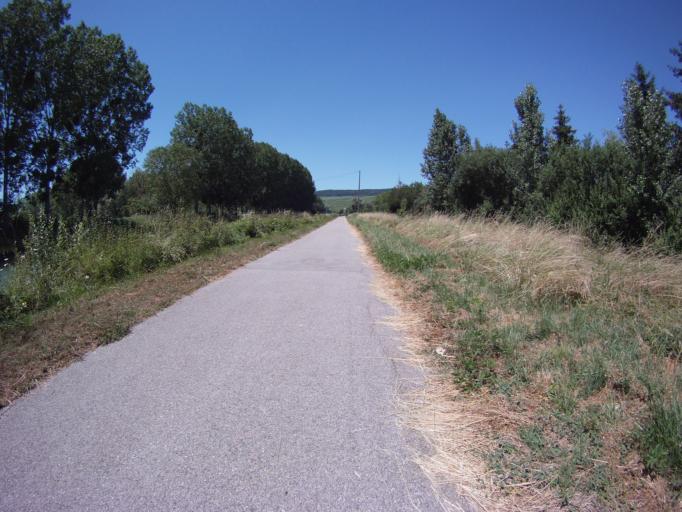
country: FR
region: Champagne-Ardenne
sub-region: Departement de la Marne
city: Epernay
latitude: 49.0687
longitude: 3.9473
